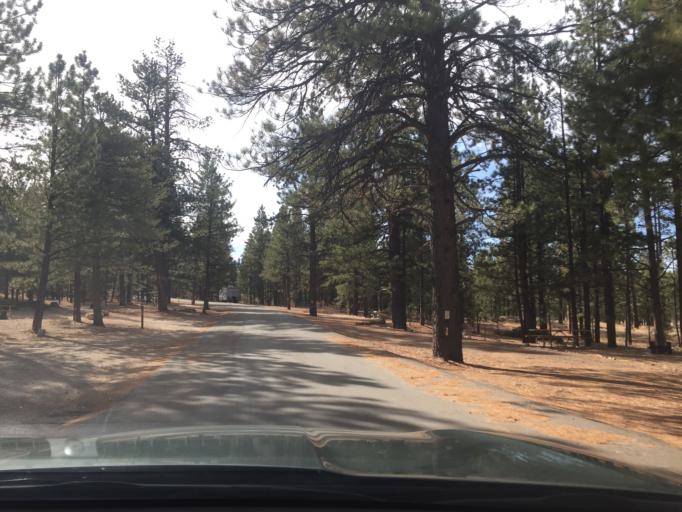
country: US
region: Utah
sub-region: Garfield County
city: Panguitch
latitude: 37.6395
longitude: -112.1679
